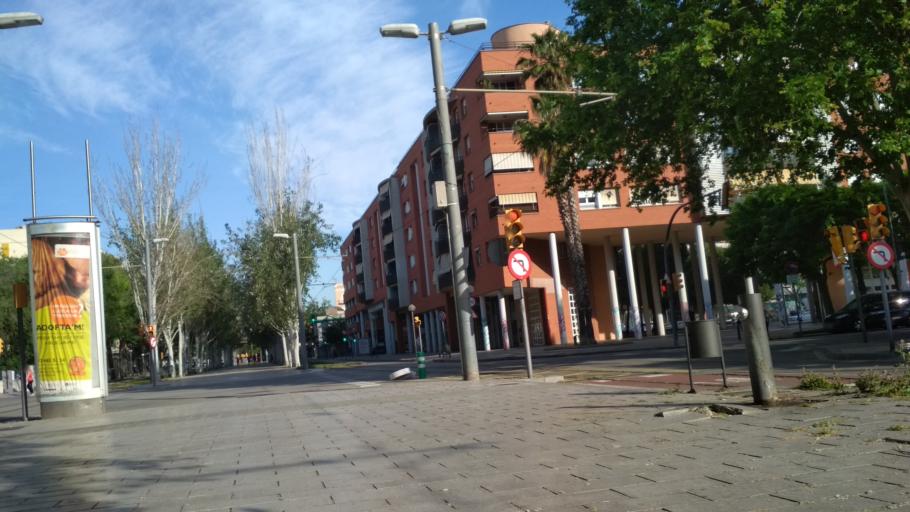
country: ES
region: Catalonia
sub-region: Provincia de Barcelona
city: Sant Adria de Besos
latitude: 41.4278
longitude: 2.2246
